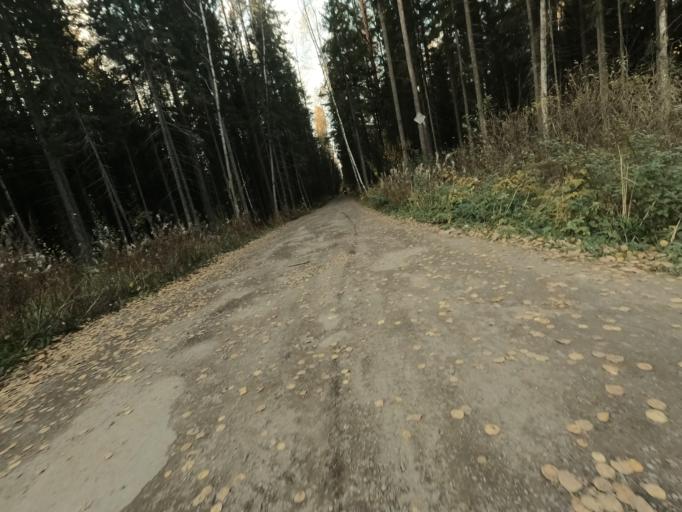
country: RU
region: St.-Petersburg
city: Solnechnoye
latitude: 60.1676
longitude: 29.9648
